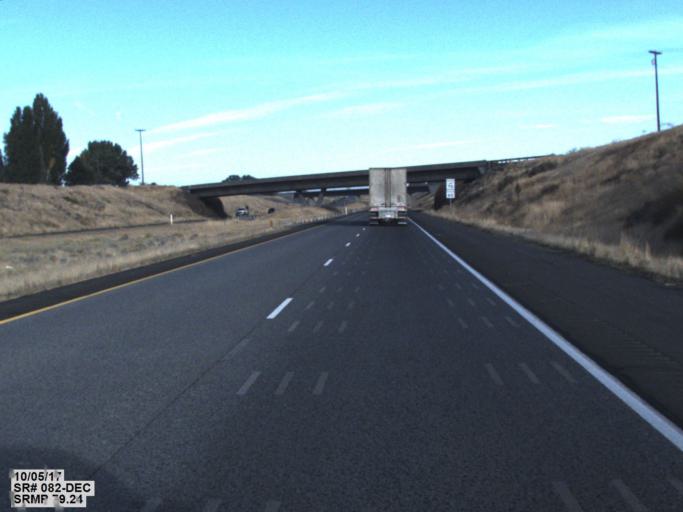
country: US
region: Washington
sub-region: Benton County
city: Prosser
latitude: 46.2277
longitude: -119.8024
